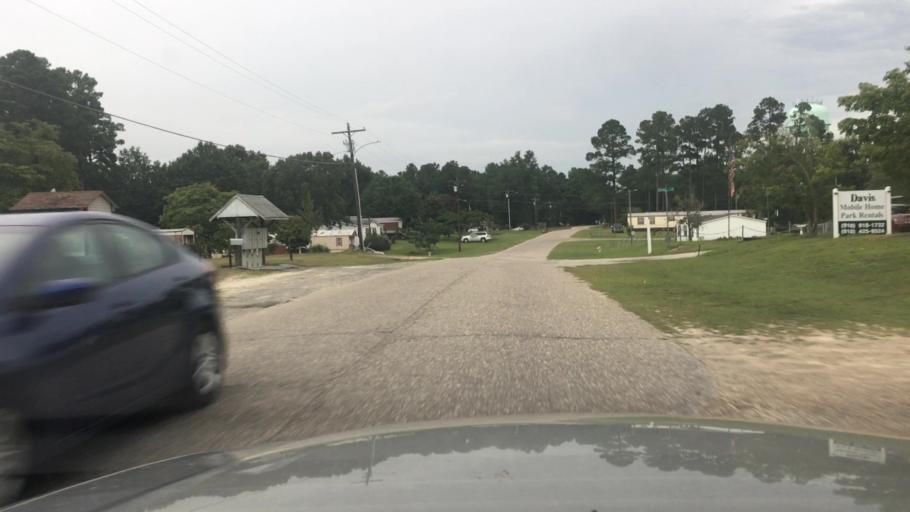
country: US
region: North Carolina
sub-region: Hoke County
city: Rockfish
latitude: 34.9826
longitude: -79.0342
